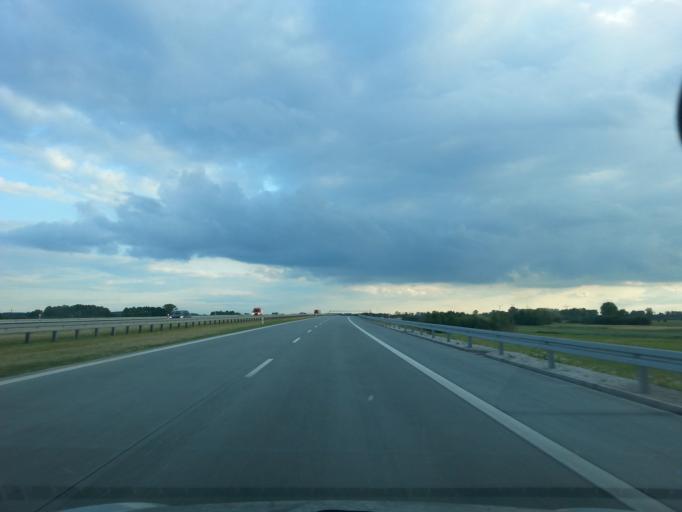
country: PL
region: Lodz Voivodeship
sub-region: Powiat sieradzki
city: Sieradz
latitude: 51.5702
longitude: 18.7830
